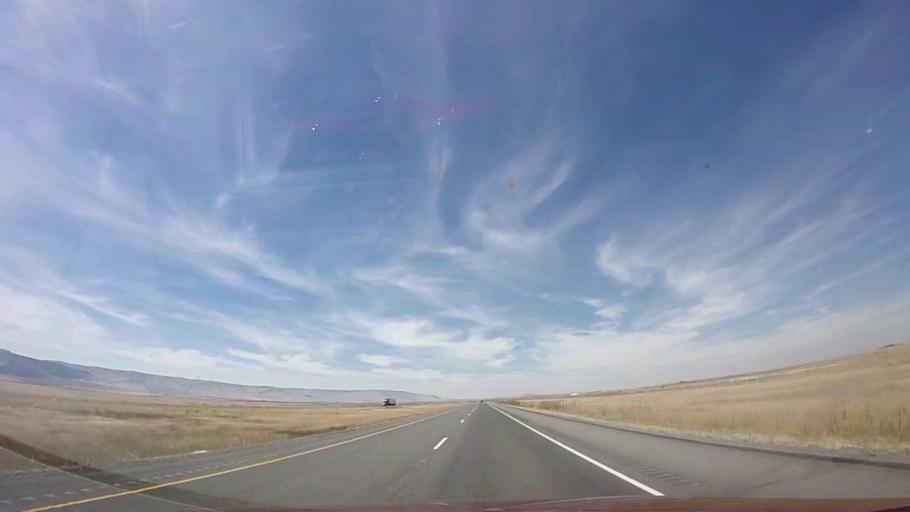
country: US
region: Idaho
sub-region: Minidoka County
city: Rupert
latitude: 42.3911
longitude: -113.2908
